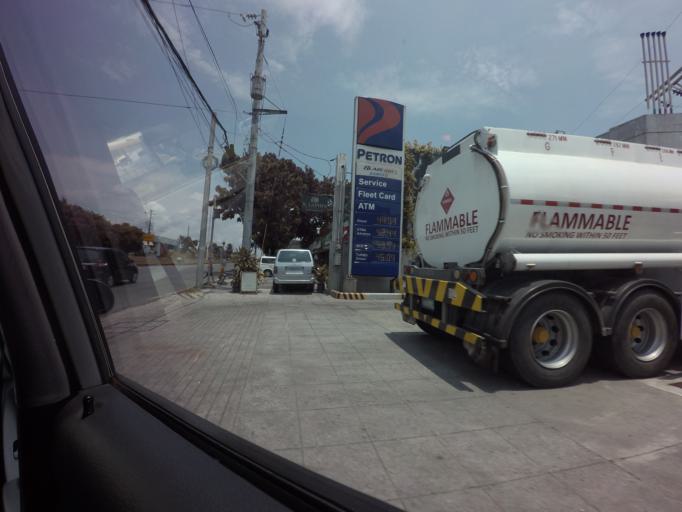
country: PH
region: Metro Manila
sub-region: City of Manila
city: Quiapo
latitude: 14.5913
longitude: 121.0017
